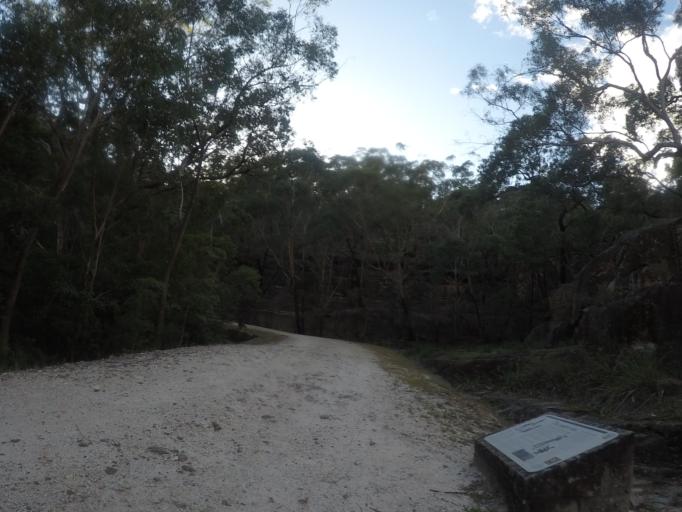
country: AU
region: New South Wales
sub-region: Hornsby Shire
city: Glenorie
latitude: -33.3684
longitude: 150.9872
